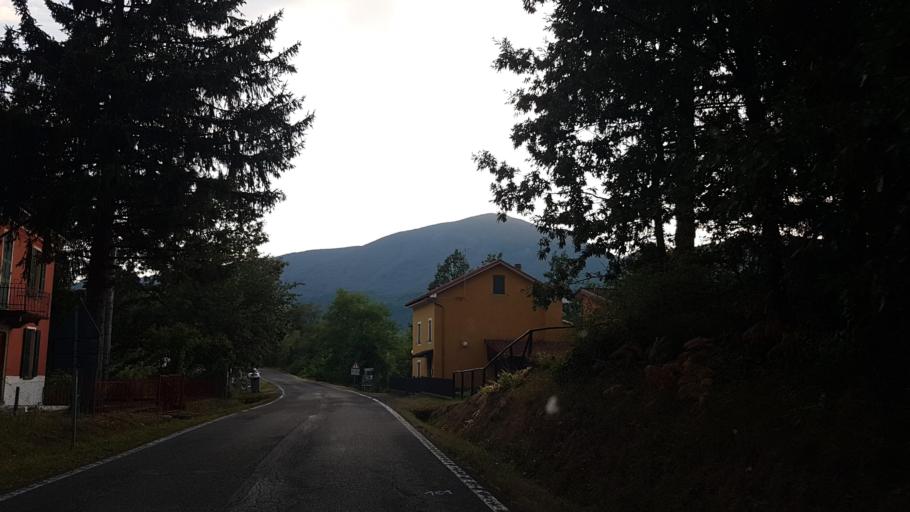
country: IT
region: Emilia-Romagna
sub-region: Provincia di Parma
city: Tornolo
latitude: 44.4466
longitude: 9.6394
